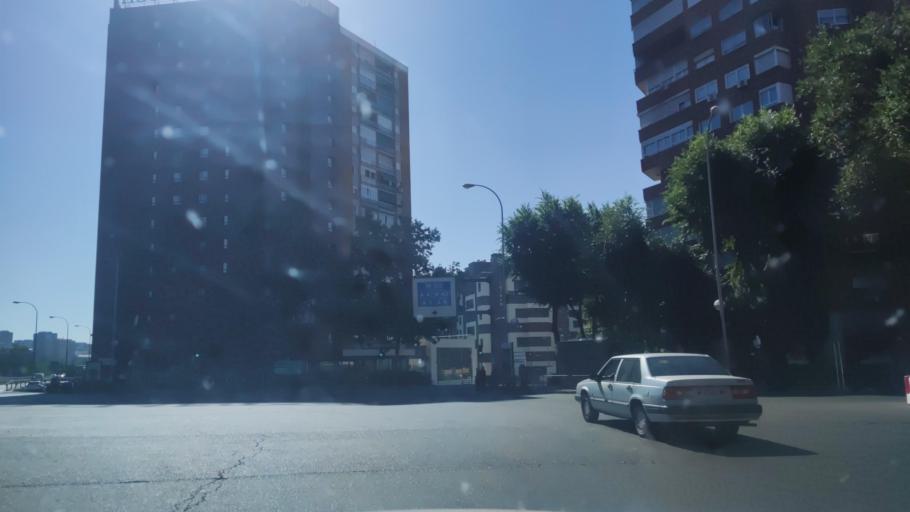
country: ES
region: Madrid
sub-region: Provincia de Madrid
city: Retiro
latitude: 40.4064
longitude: -3.6704
